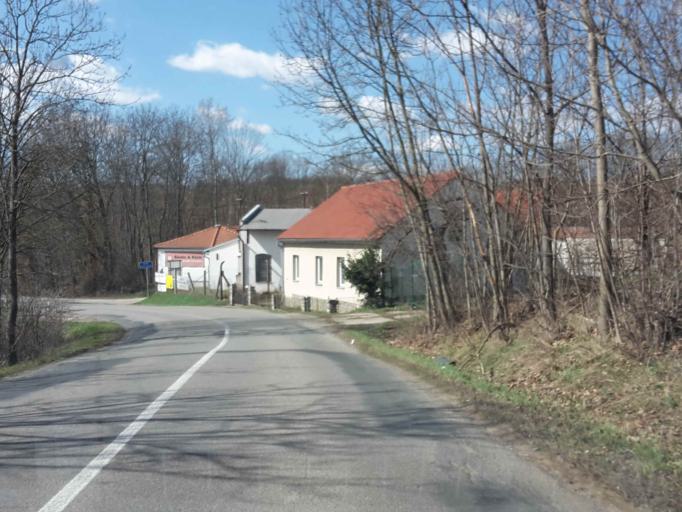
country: CZ
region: South Moravian
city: Bilovice nad Svitavou
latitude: 49.2422
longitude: 16.6561
